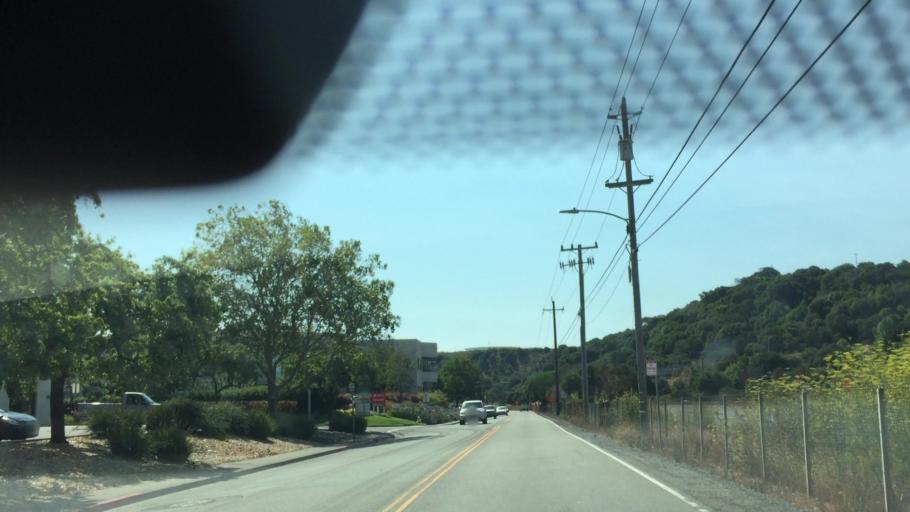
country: US
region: California
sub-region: Marin County
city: Corte Madera
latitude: 37.9494
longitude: -122.4939
